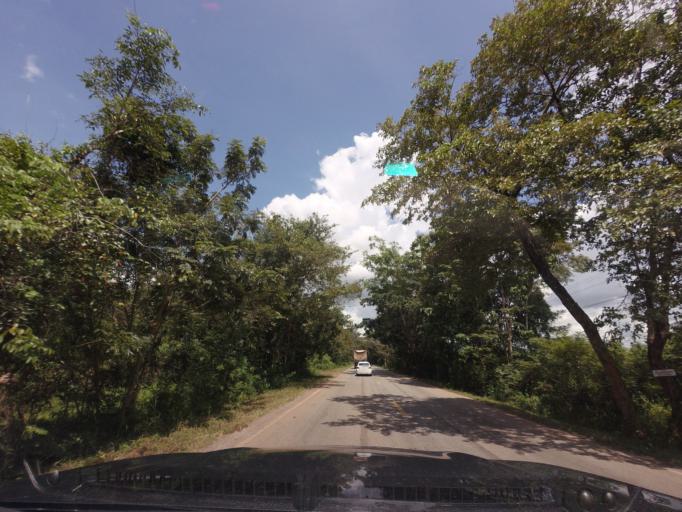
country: TH
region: Changwat Udon Thani
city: Phibun Rak
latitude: 17.5839
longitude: 103.0405
